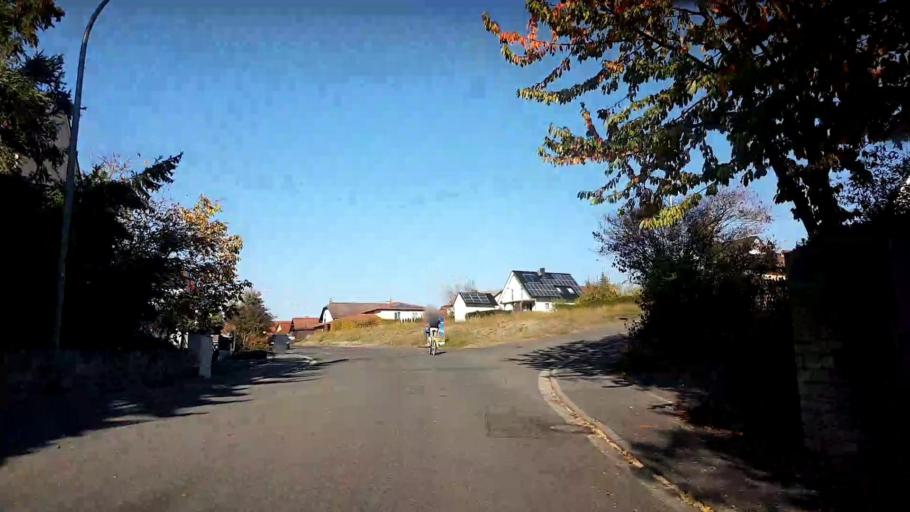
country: DE
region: Bavaria
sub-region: Upper Franconia
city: Walsdorf
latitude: 49.8721
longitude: 10.7840
